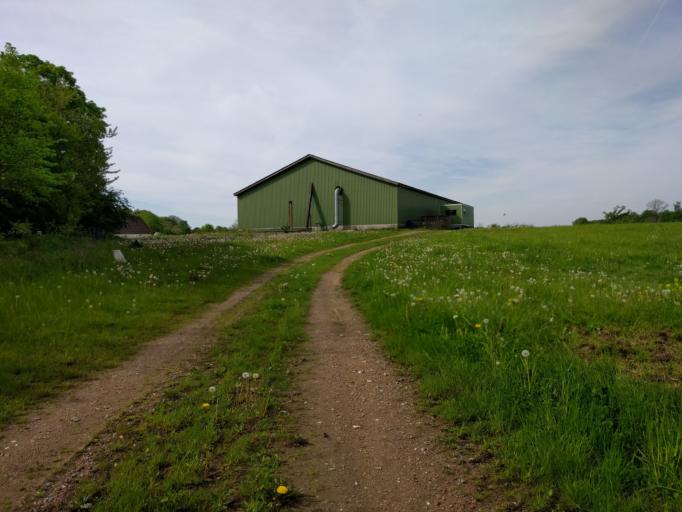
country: DK
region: South Denmark
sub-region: Odense Kommune
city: Bullerup
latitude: 55.4012
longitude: 10.4959
